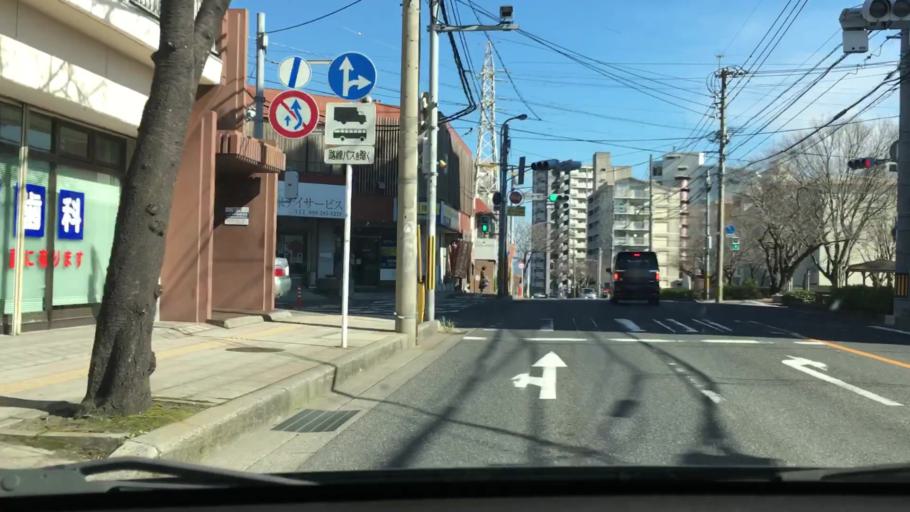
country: JP
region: Kagoshima
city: Kagoshima-shi
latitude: 31.5623
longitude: 130.5352
